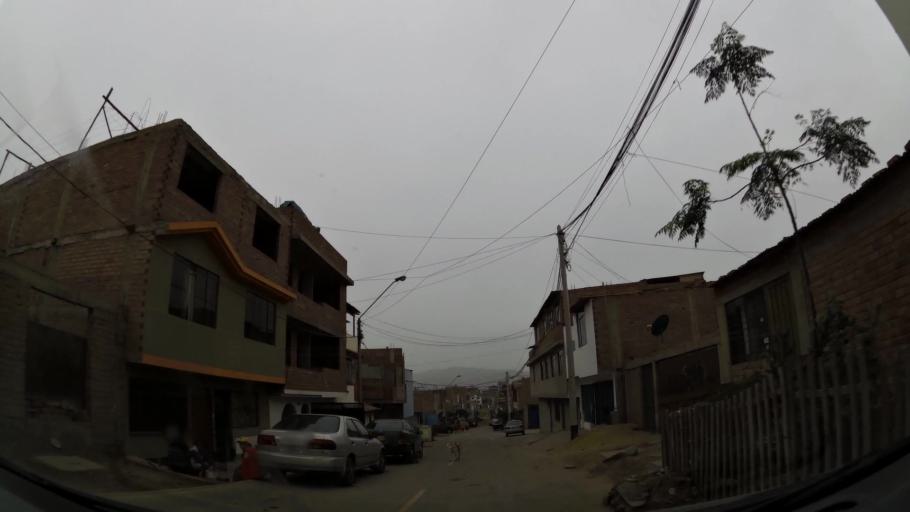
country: PE
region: Lima
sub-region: Lima
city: Surco
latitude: -12.1878
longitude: -76.9833
